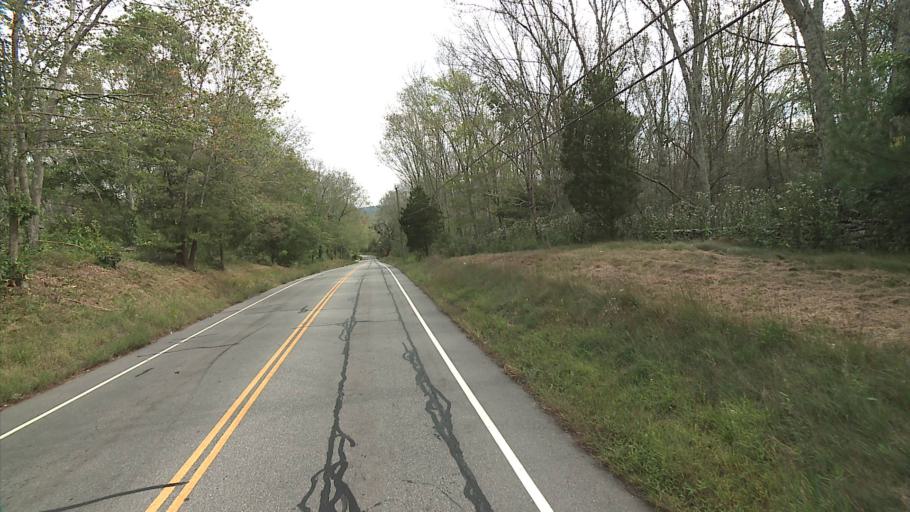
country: US
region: Connecticut
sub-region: New London County
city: Jewett City
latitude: 41.6520
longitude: -71.9766
